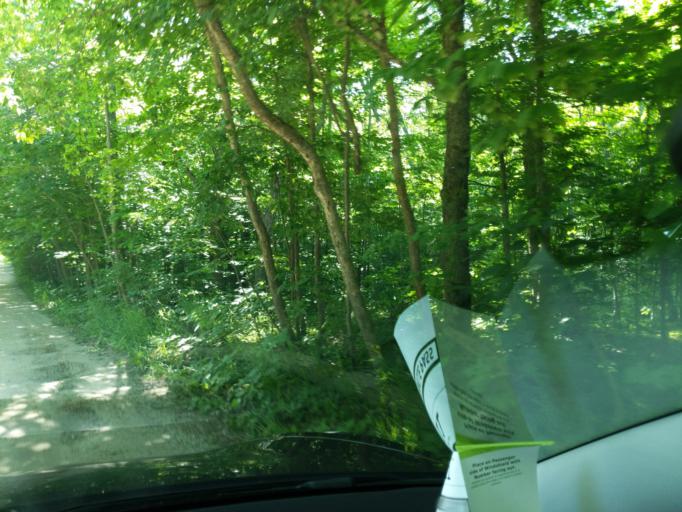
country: US
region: Michigan
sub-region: Mackinac County
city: Saint Ignace
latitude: 45.6984
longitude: -84.7305
